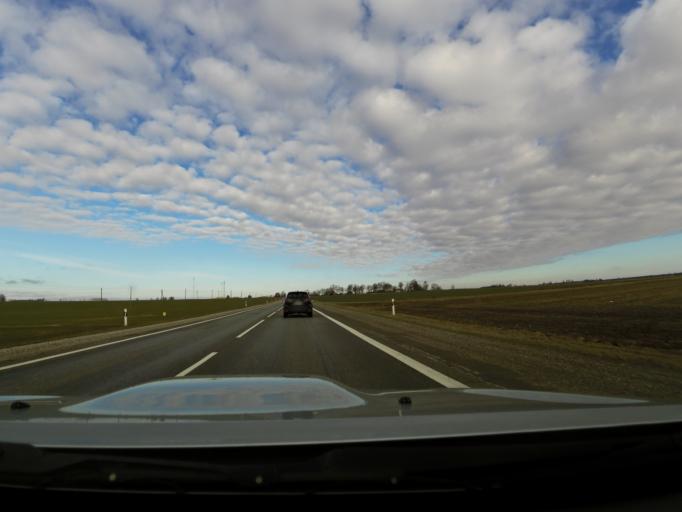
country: LT
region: Siauliu apskritis
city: Pakruojis
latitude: 55.7836
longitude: 24.0417
